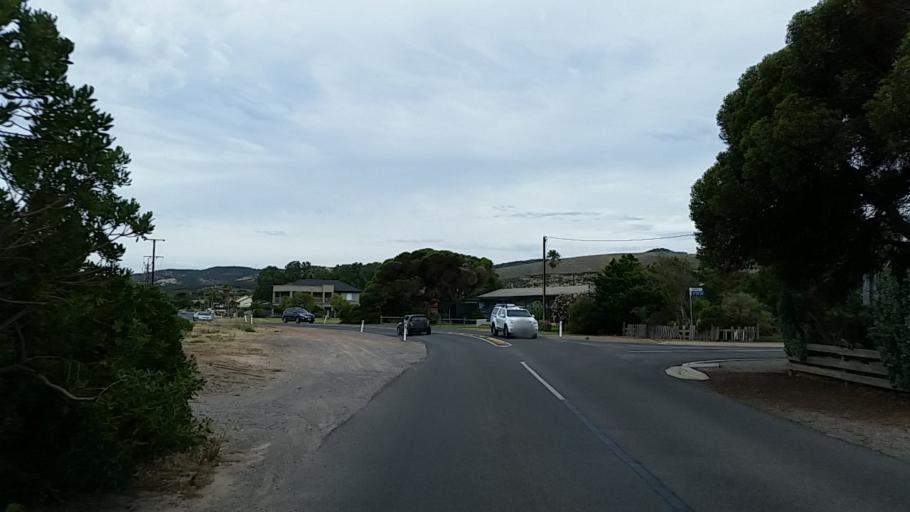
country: AU
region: South Australia
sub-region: Onkaparinga
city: Port Willunga
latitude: -35.3296
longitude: 138.4490
